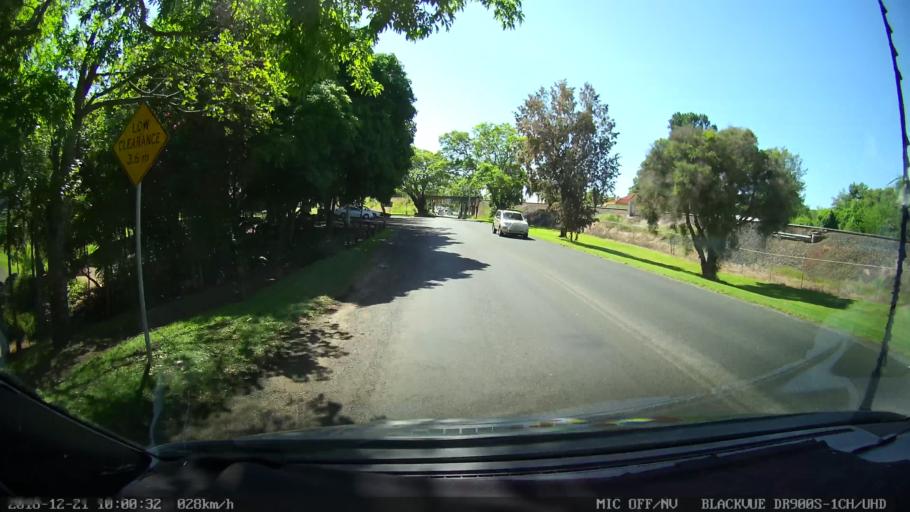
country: AU
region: New South Wales
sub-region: Clarence Valley
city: Grafton
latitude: -29.6841
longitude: 152.9263
